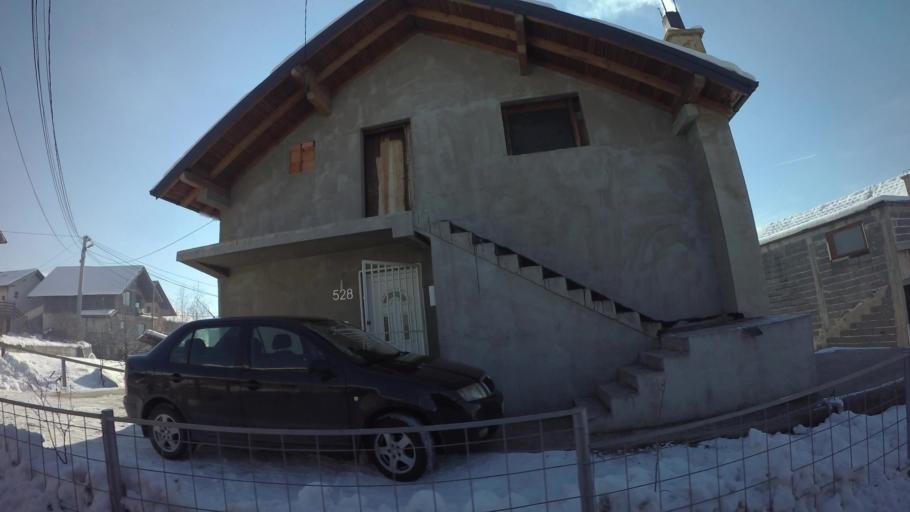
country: BA
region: Federation of Bosnia and Herzegovina
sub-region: Kanton Sarajevo
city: Sarajevo
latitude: 43.8392
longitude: 18.3692
